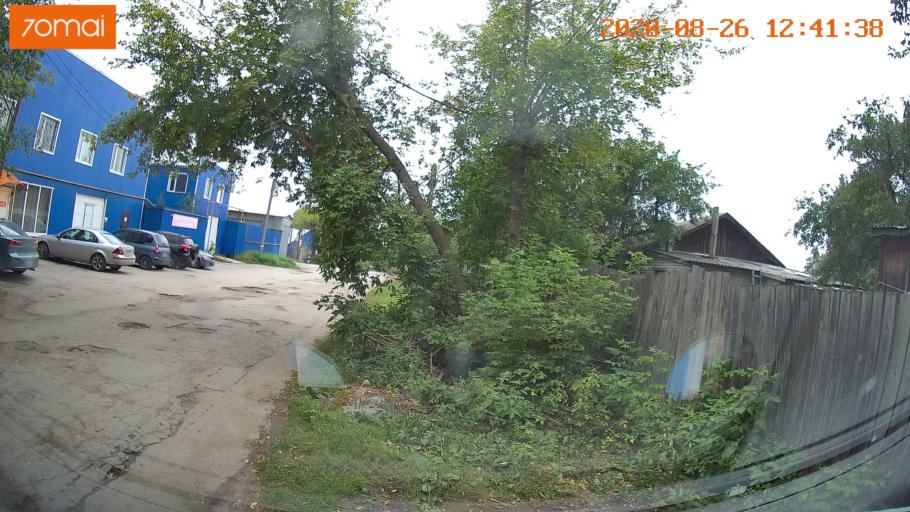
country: RU
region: Rjazan
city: Ryazan'
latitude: 54.5994
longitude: 39.7589
